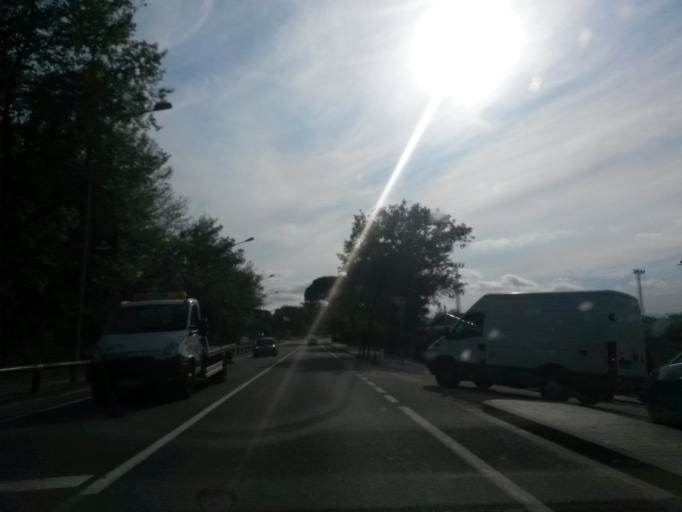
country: ES
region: Catalonia
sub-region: Provincia de Girona
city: Caldes de Malavella
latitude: 41.8382
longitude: 2.8006
